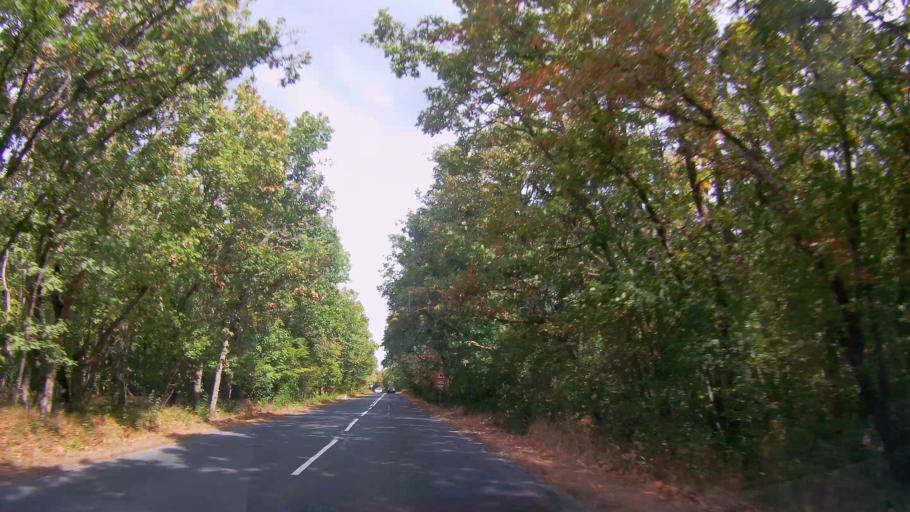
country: BG
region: Burgas
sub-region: Obshtina Primorsko
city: Primorsko
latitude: 42.2894
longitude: 27.7350
